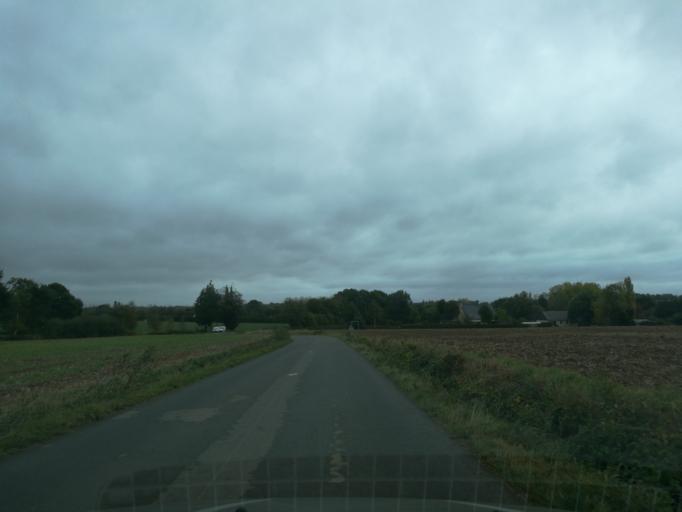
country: FR
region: Brittany
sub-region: Departement d'Ille-et-Vilaine
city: Pleumeleuc
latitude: 48.1838
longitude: -1.9079
